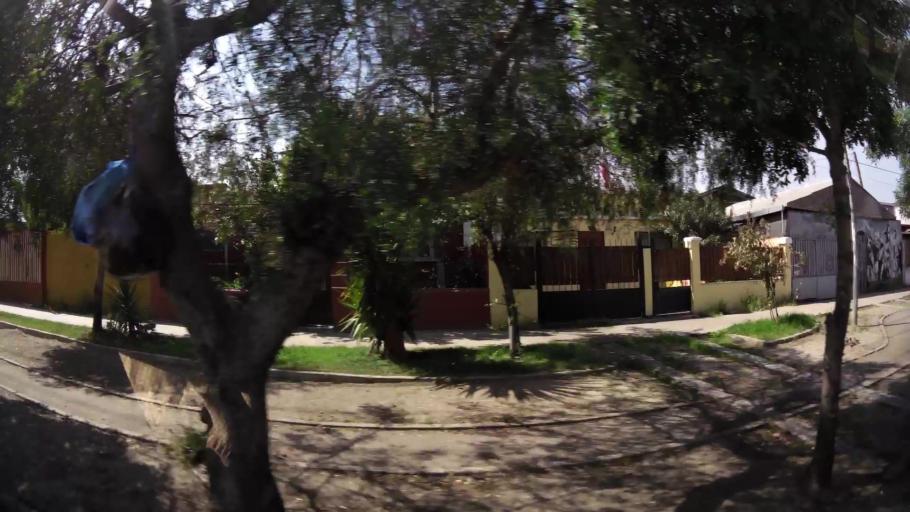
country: CL
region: Santiago Metropolitan
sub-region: Provincia de Santiago
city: Lo Prado
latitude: -33.4372
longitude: -70.7308
